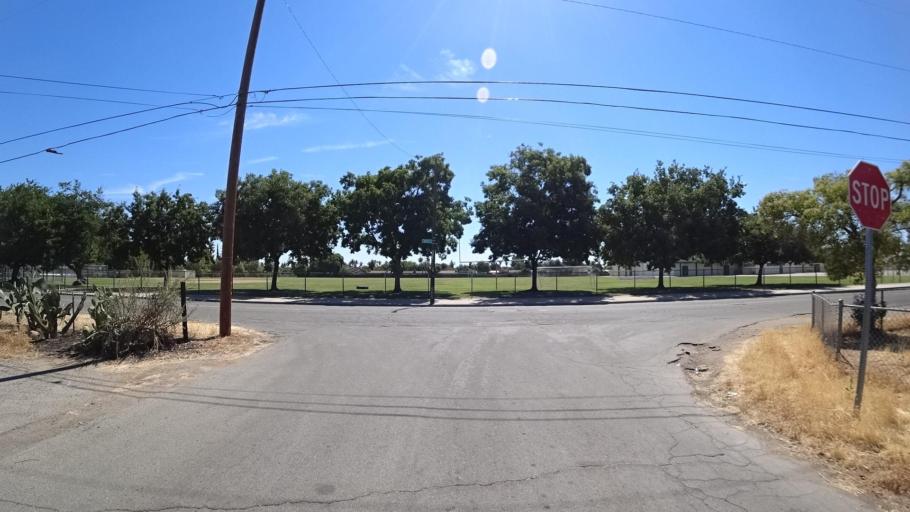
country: US
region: California
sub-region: Fresno County
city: Sunnyside
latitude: 36.7459
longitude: -119.7230
